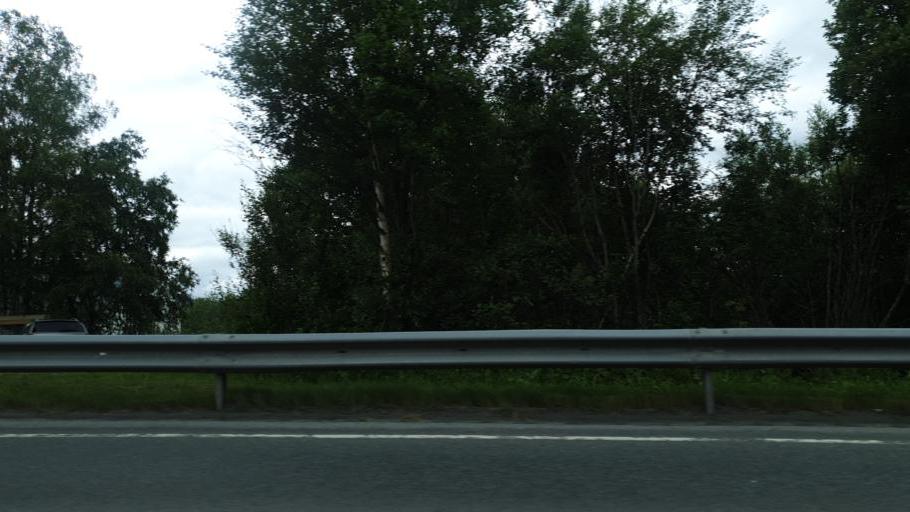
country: NO
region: Sor-Trondelag
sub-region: Rennebu
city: Berkak
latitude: 62.8266
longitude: 10.0081
